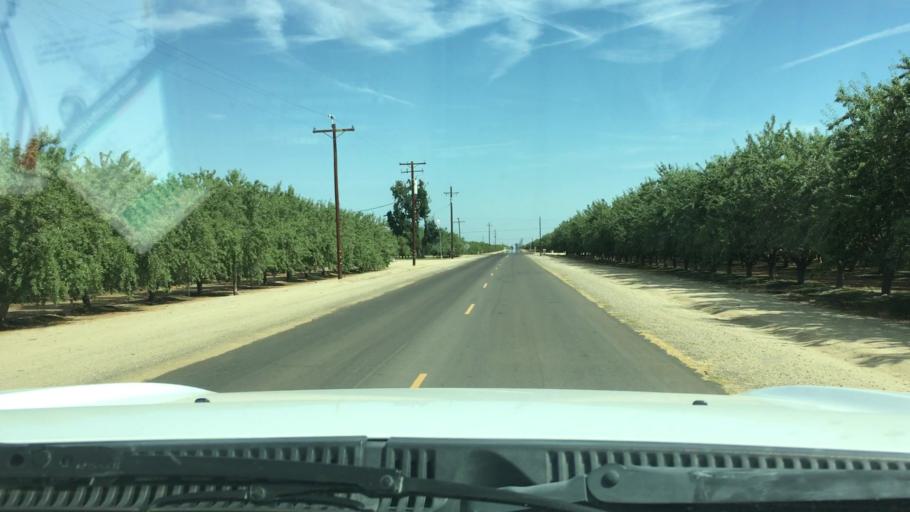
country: US
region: California
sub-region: Kern County
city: Wasco
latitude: 35.5269
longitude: -119.3499
